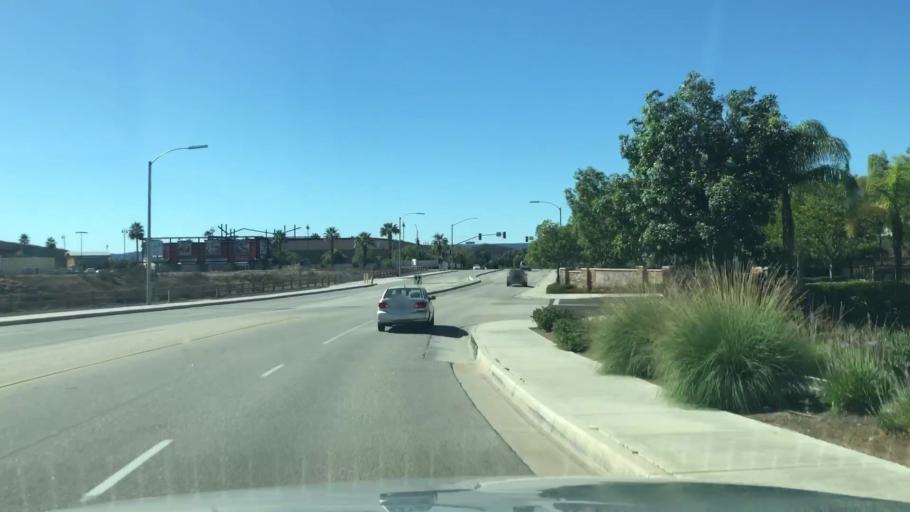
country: US
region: California
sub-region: Riverside County
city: Murrieta Hot Springs
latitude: 33.6020
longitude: -117.1760
